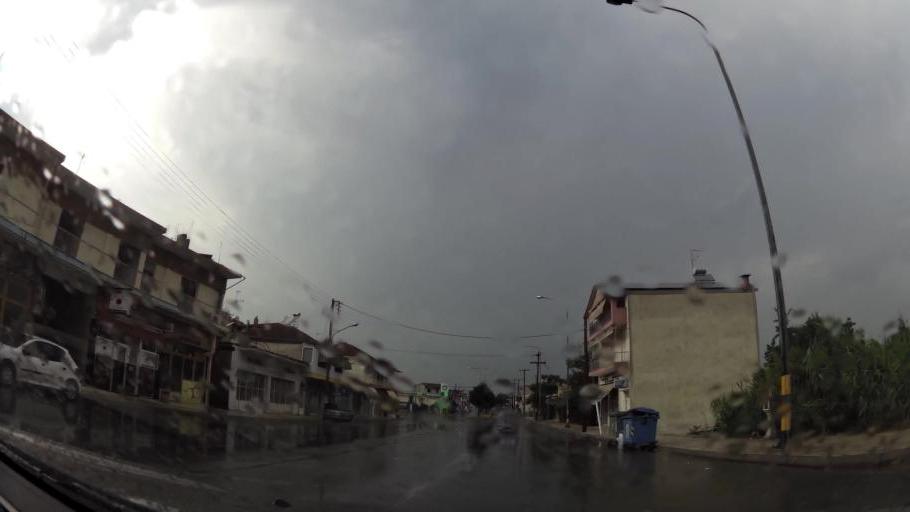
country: GR
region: Central Macedonia
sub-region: Nomos Imathias
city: Veroia
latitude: 40.5370
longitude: 22.2025
